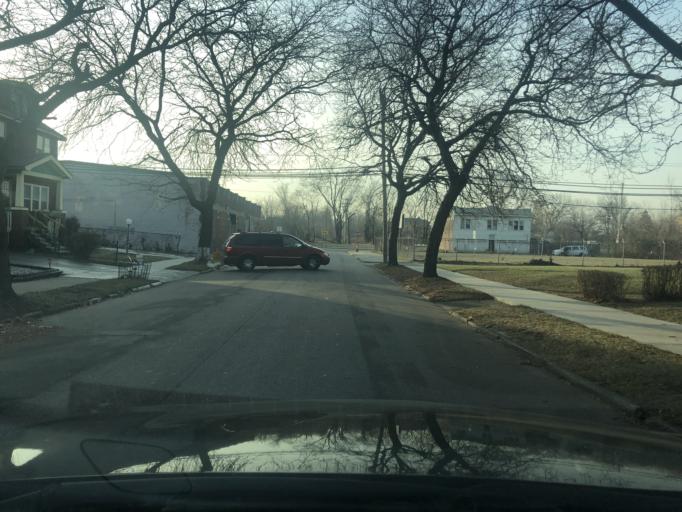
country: US
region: Michigan
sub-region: Wayne County
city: Highland Park
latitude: 42.4037
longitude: -83.1314
